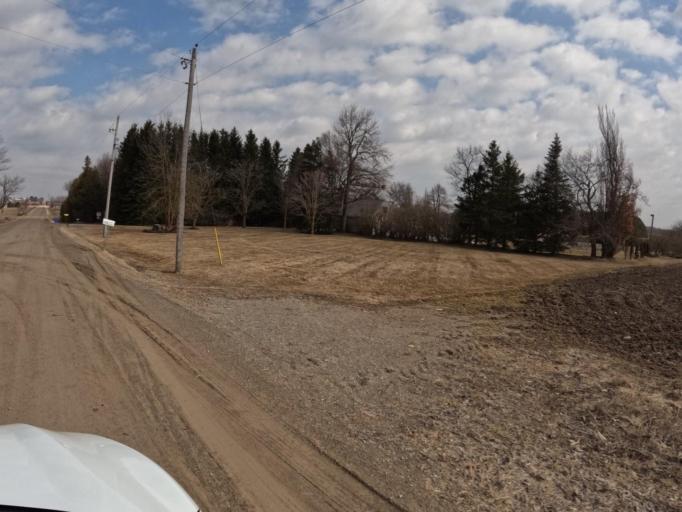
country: CA
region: Ontario
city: Orangeville
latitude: 43.9197
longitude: -80.2393
